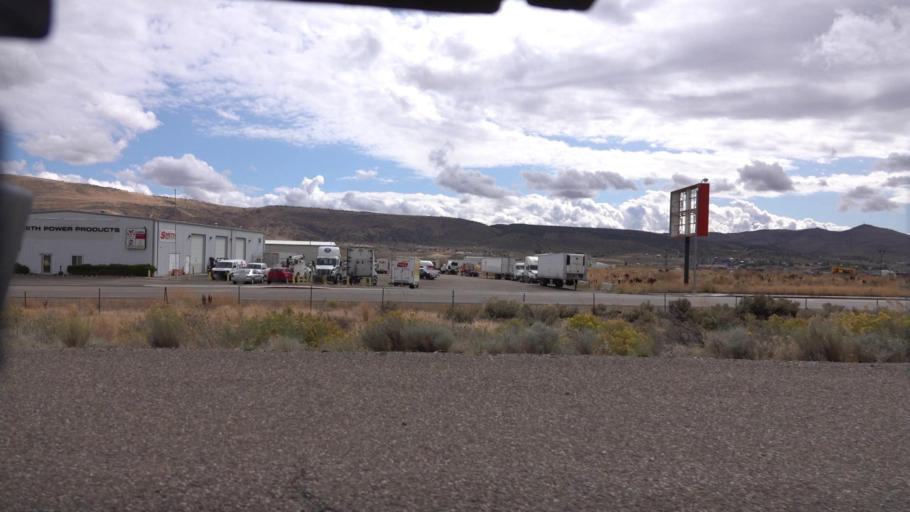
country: US
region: Nevada
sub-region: Elko County
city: Elko
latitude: 40.8717
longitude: -115.7261
